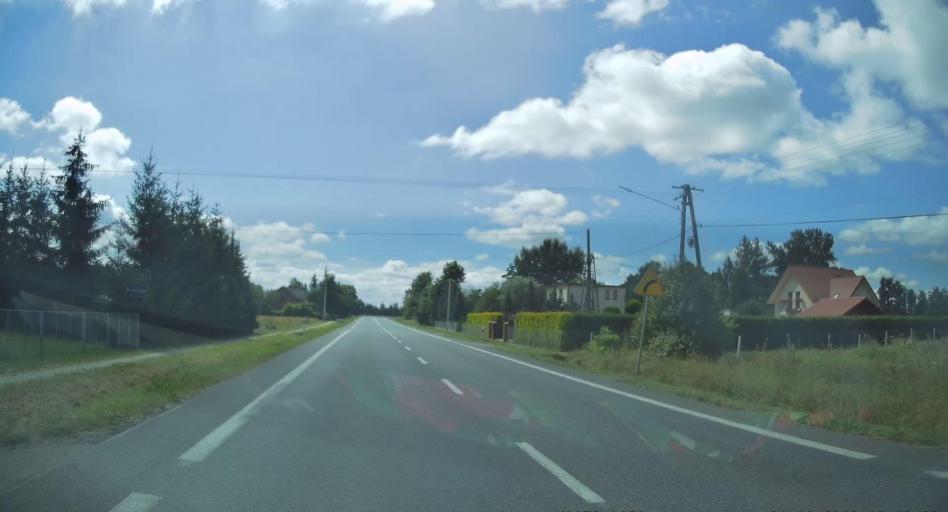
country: PL
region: Subcarpathian Voivodeship
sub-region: Powiat mielecki
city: Przeclaw
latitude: 50.1636
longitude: 21.4878
